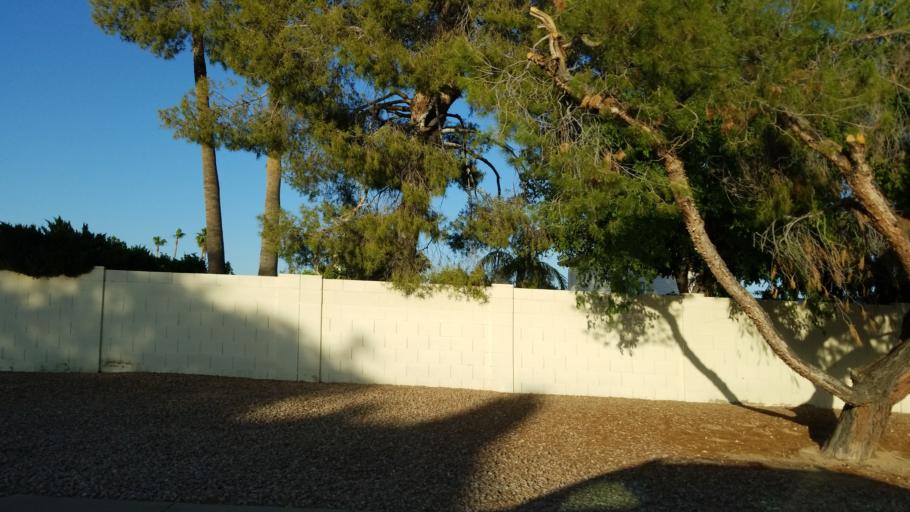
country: US
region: Arizona
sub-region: Maricopa County
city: Scottsdale
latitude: 33.5108
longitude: -111.9174
